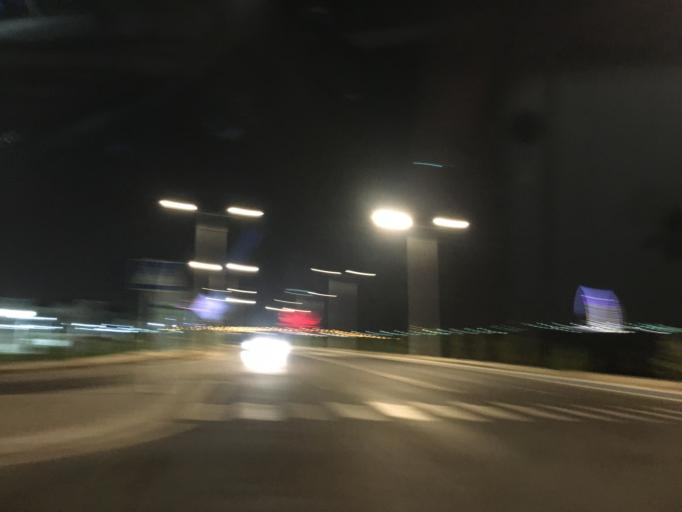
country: TM
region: Ahal
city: Ashgabat
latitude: 37.9413
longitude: 58.3449
